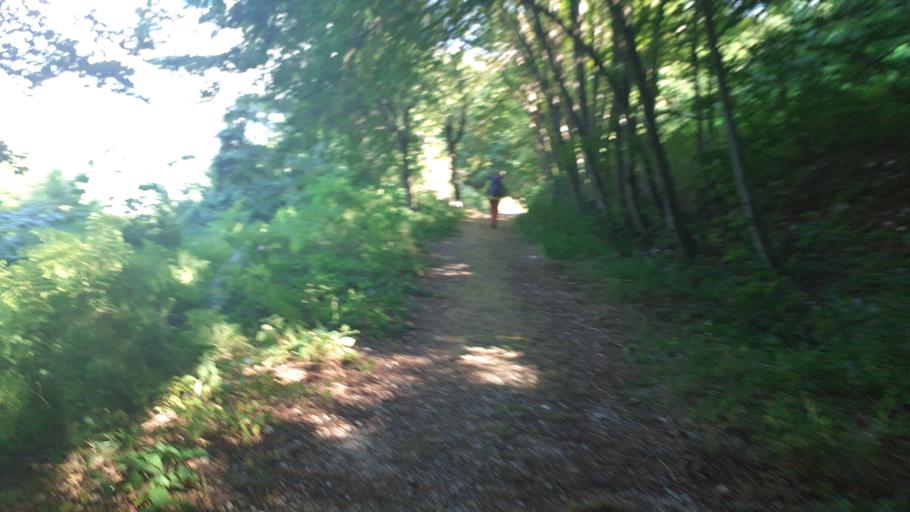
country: IT
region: Abruzzo
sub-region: Provincia di Pescara
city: Sant'Eufemia a Maiella
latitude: 42.1102
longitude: 13.9982
